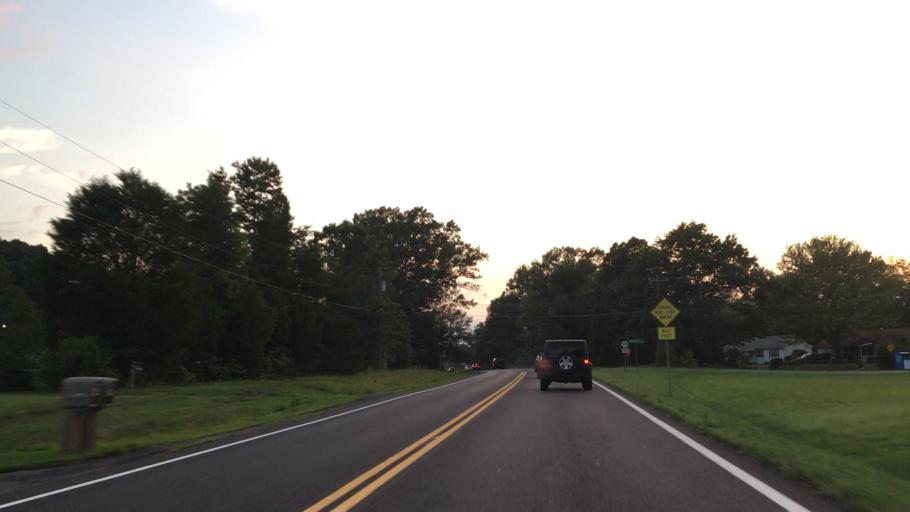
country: US
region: Virginia
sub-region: Orange County
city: Orange
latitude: 38.2691
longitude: -77.9445
